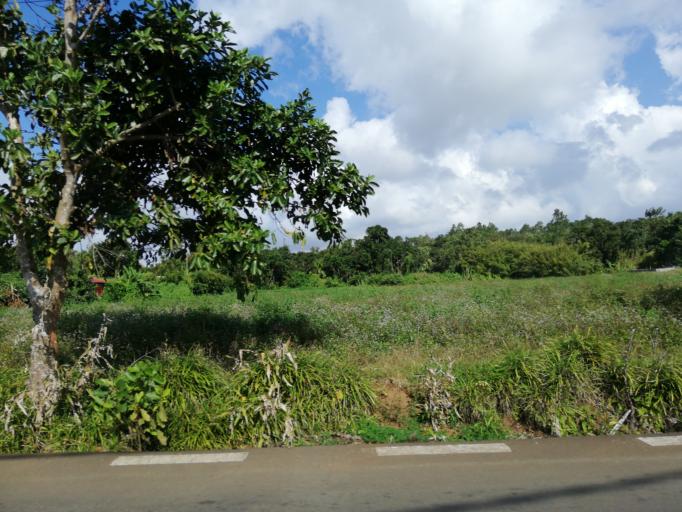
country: MU
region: Pamplemousses
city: Creve Coeur
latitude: -20.2095
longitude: 57.5641
